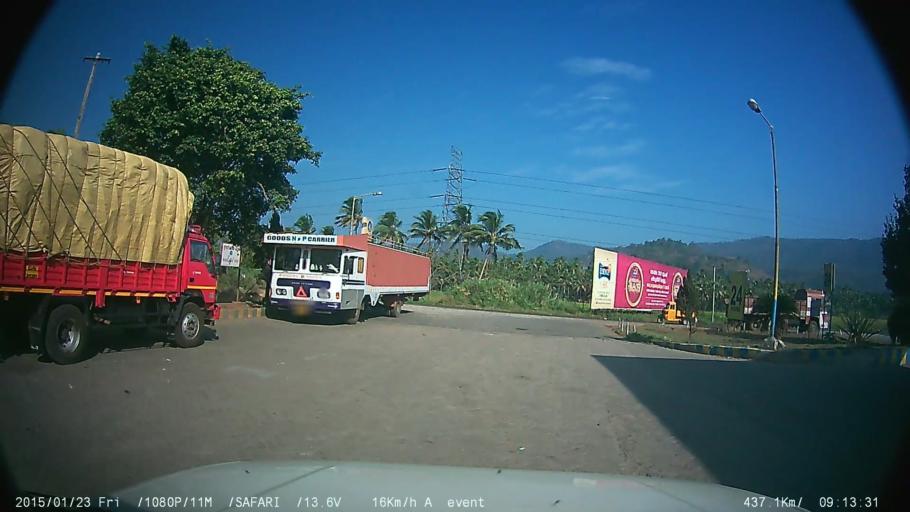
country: IN
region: Kerala
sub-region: Thrissur District
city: Trichur
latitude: 10.5543
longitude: 76.3185
